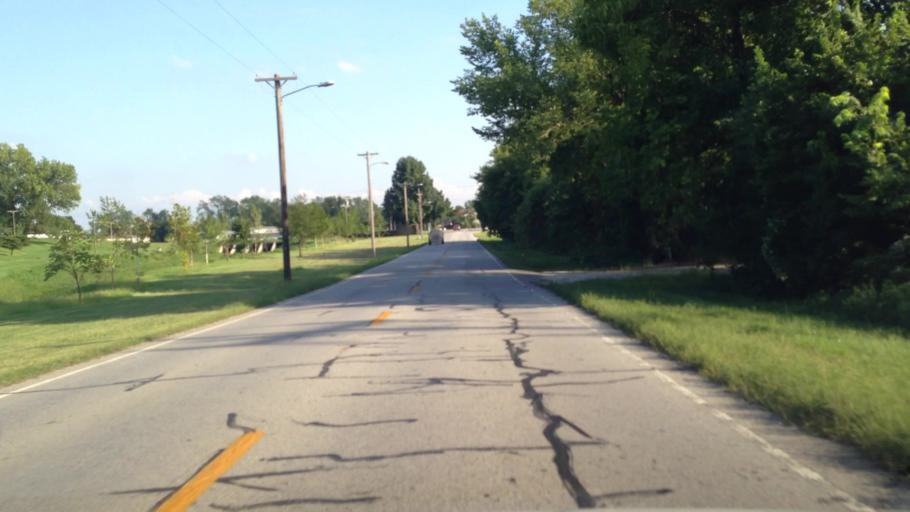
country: US
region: Missouri
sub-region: Jasper County
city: Joplin
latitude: 37.0900
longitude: -94.5084
